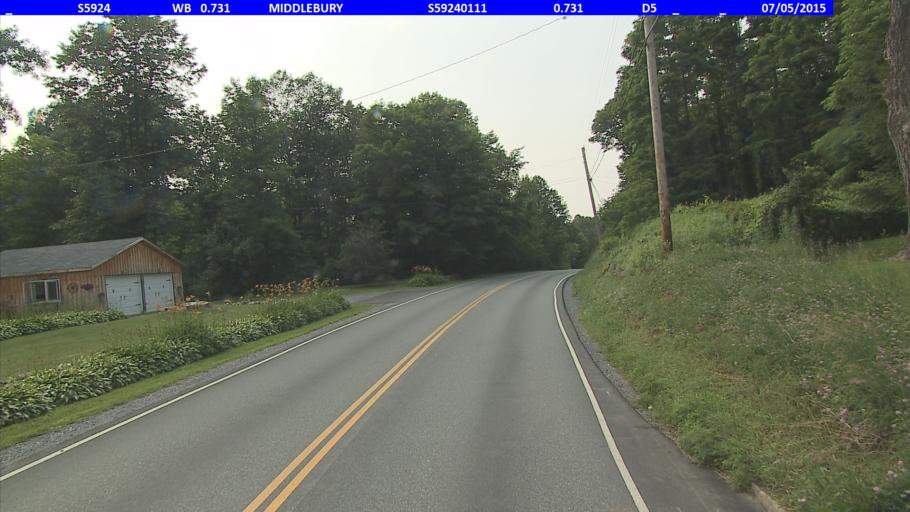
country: US
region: Vermont
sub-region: Addison County
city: Middlebury (village)
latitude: 44.0136
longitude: -73.1478
